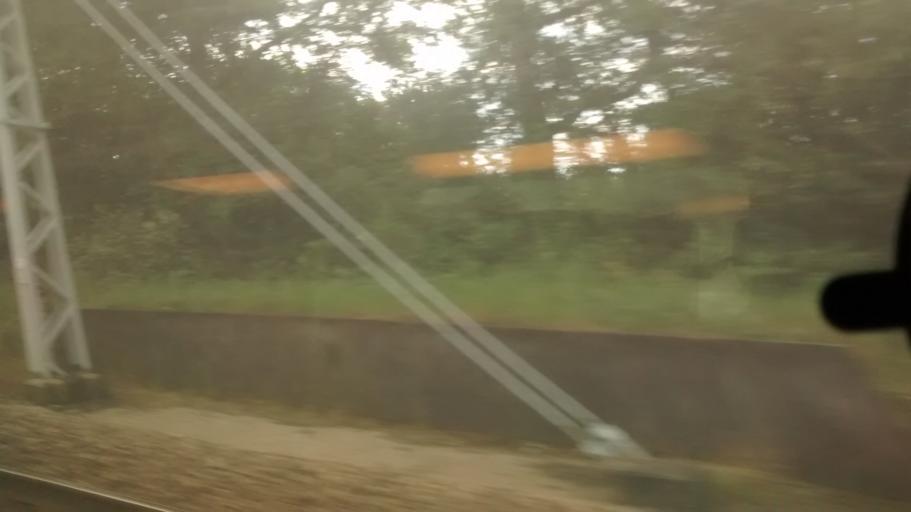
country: FR
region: Pays de la Loire
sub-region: Departement de la Sarthe
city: Champagne
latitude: 48.0129
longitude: 0.3122
